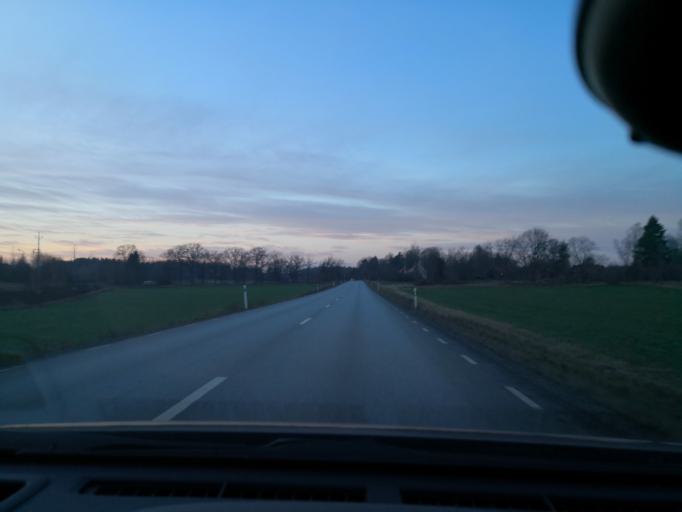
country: SE
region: Vaestmanland
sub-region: Arboga Kommun
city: Arboga
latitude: 59.4106
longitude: 15.7904
